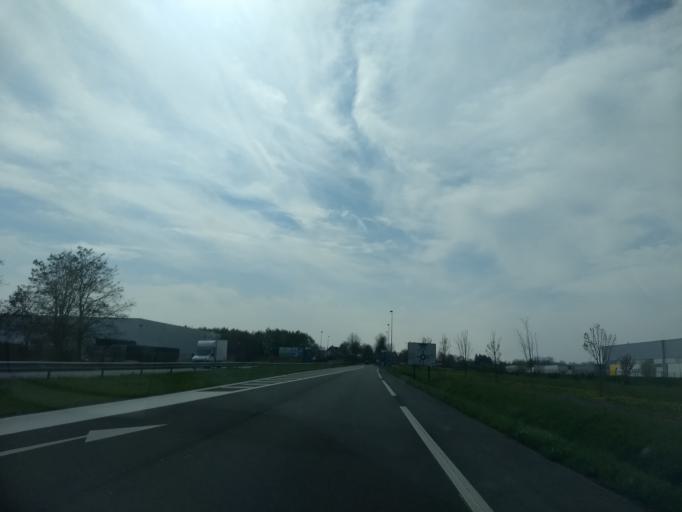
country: FR
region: Nord-Pas-de-Calais
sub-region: Departement du Pas-de-Calais
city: Brebieres
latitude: 50.3445
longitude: 3.0309
